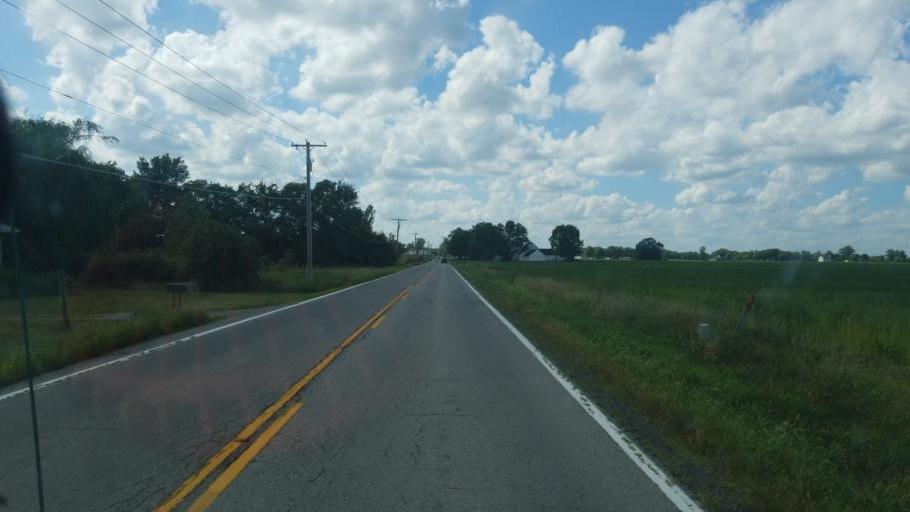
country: US
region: Ohio
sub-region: Union County
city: Richwood
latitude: 40.3953
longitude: -83.2731
